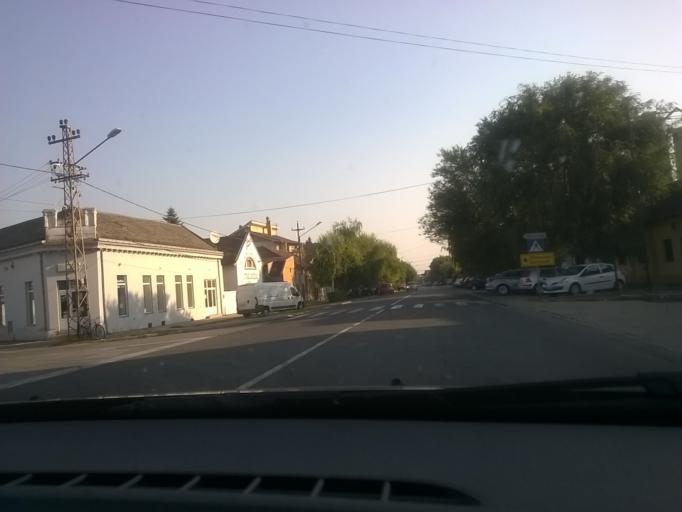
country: RS
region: Autonomna Pokrajina Vojvodina
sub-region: Juznobanatski Okrug
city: Vrsac
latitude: 45.1116
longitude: 21.2845
